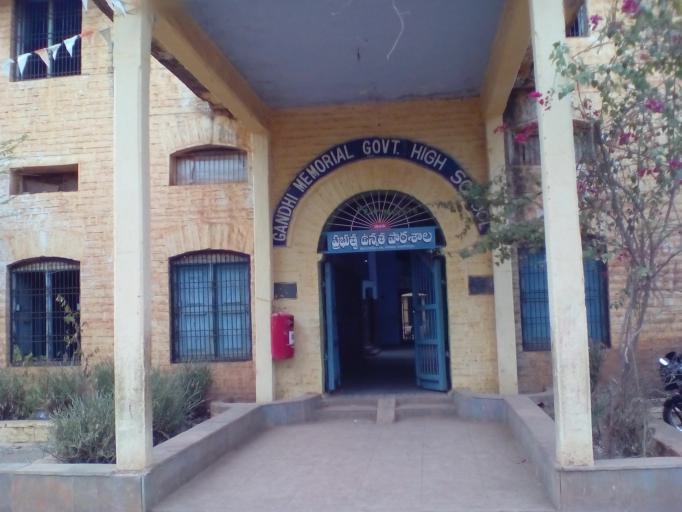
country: IN
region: Andhra Pradesh
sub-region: Kurnool
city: Nandikotkur
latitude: 15.8515
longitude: 78.2684
